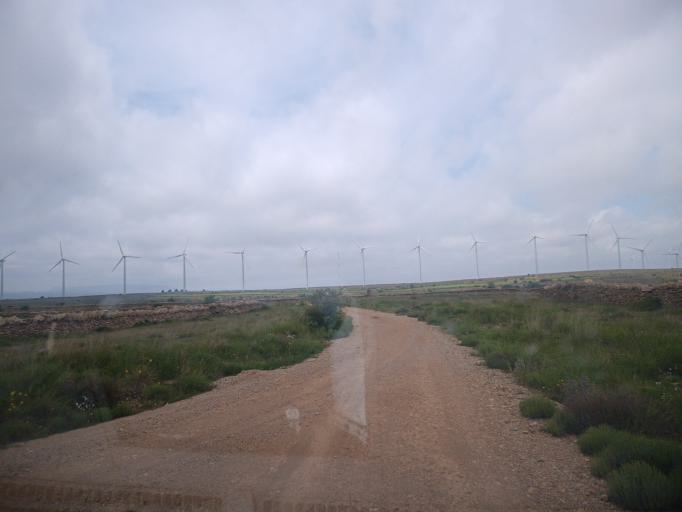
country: ES
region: Valencia
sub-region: Provincia de Castello
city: Castellfort
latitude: 40.4659
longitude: -0.1972
